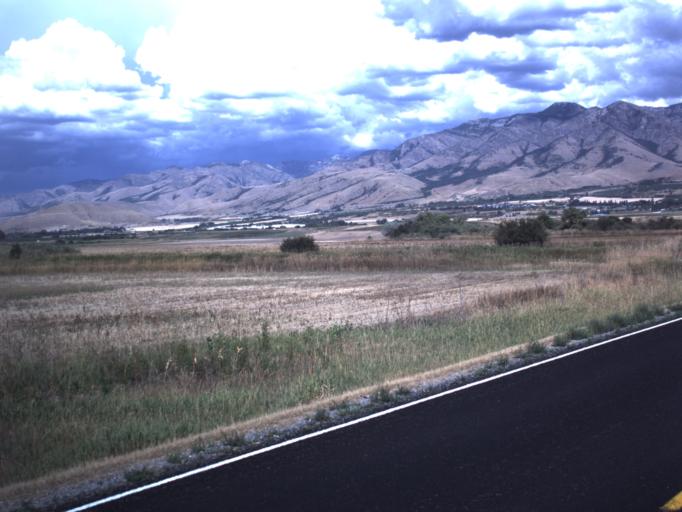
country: US
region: Utah
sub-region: Cache County
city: Richmond
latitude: 41.9246
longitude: -111.8492
